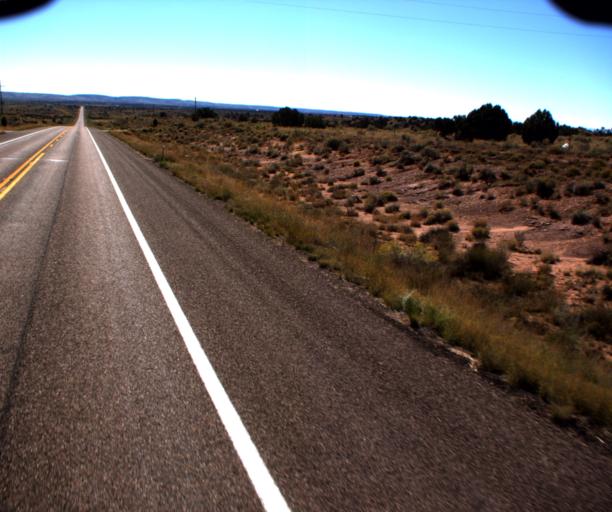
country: US
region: Arizona
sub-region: Apache County
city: Saint Johns
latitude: 34.6378
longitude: -109.6888
